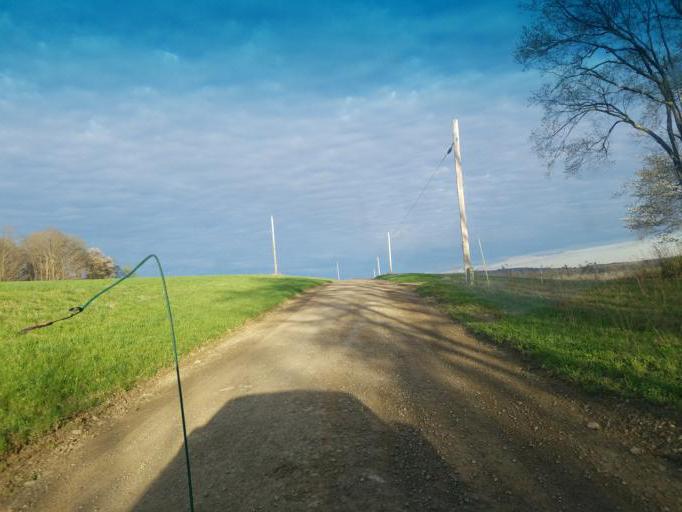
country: US
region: Pennsylvania
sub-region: Potter County
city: Galeton
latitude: 41.9018
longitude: -77.7347
